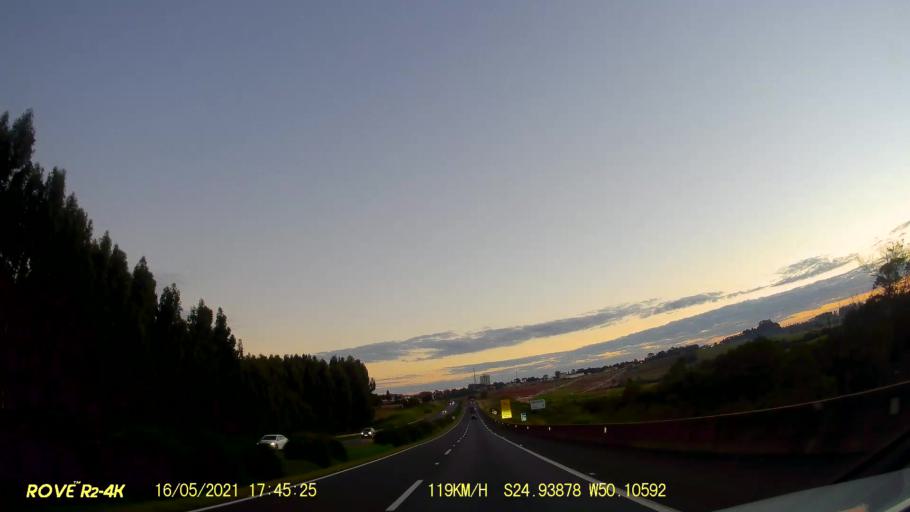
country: BR
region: Parana
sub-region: Carambei
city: Carambei
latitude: -24.9385
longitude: -50.1055
